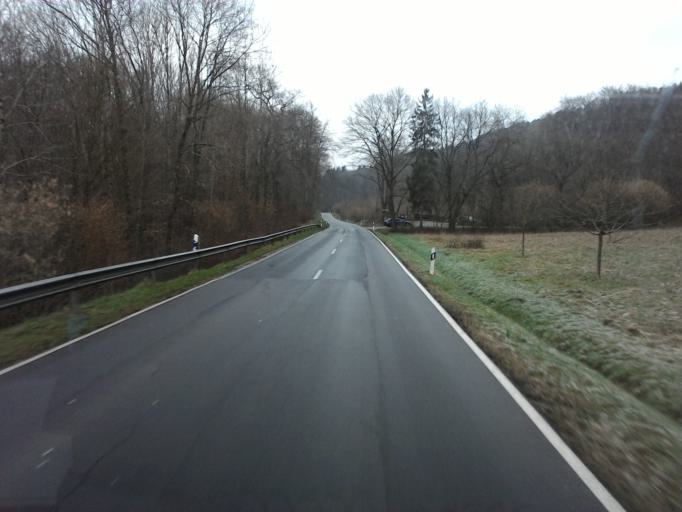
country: DE
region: Rheinland-Pfalz
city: Prumzurlay
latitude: 49.8537
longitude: 6.4470
